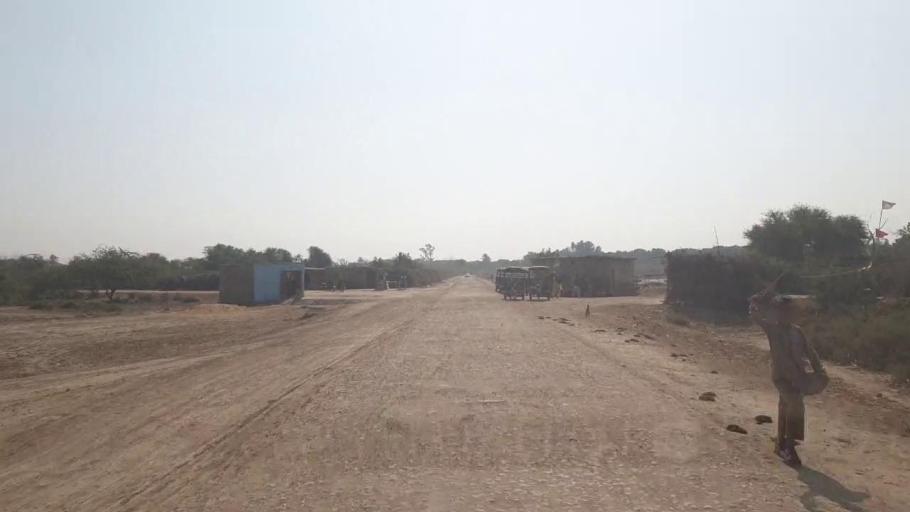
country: PK
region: Sindh
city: Tando Allahyar
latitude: 25.4530
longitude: 68.8197
